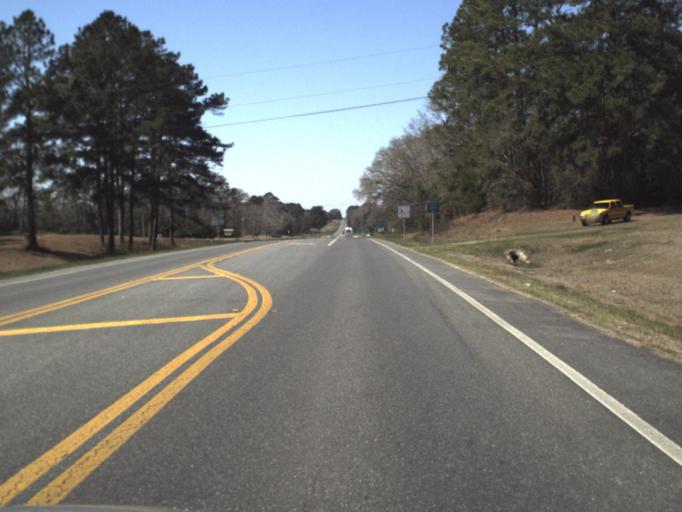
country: US
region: Florida
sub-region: Jackson County
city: Marianna
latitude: 30.7845
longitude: -85.2907
